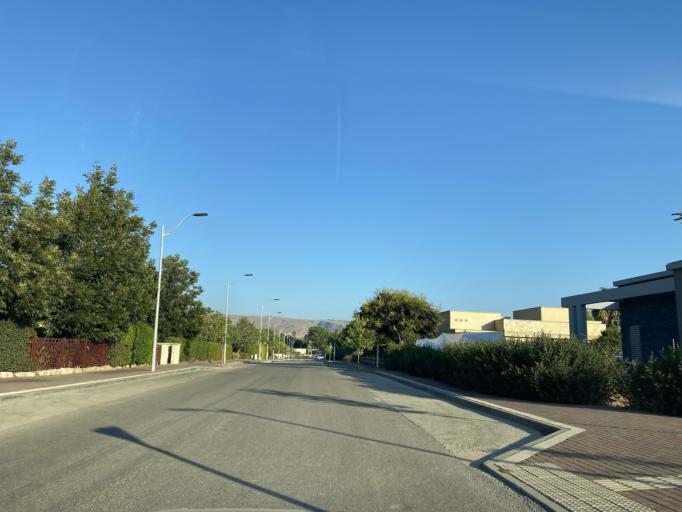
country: IL
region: Northern District
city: Qiryat Shemona
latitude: 33.1762
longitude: 35.6044
